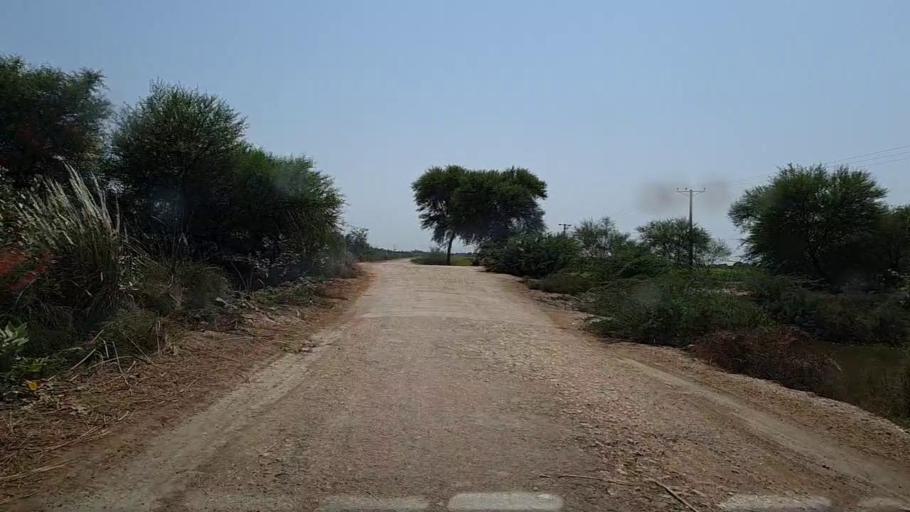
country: PK
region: Sindh
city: Mirpur Batoro
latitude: 24.6408
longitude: 68.4522
